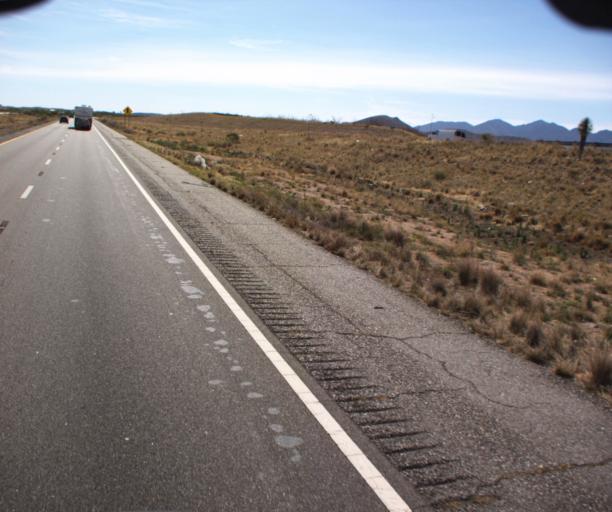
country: US
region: Arizona
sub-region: Cochise County
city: Mescal
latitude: 31.9815
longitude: -110.5355
